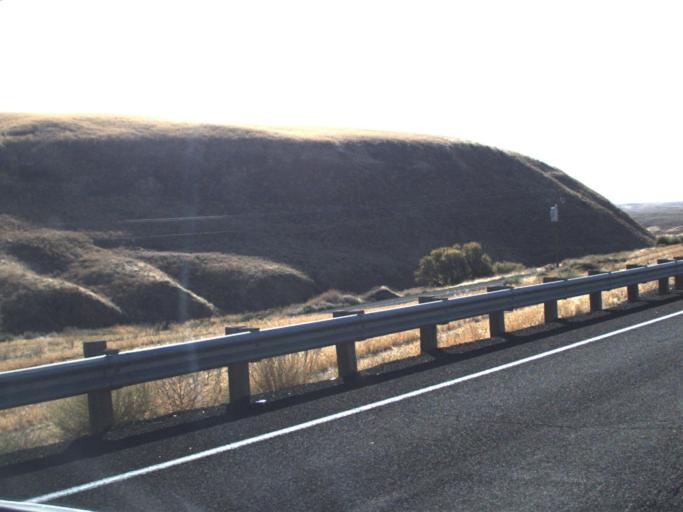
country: US
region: Washington
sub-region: Walla Walla County
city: Garrett
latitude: 46.2907
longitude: -118.5219
